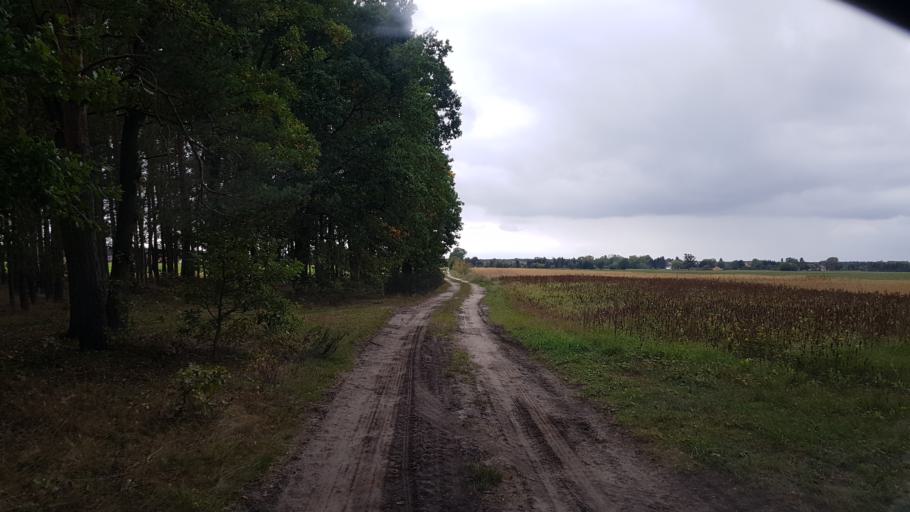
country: DE
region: Brandenburg
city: Finsterwalde
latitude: 51.5772
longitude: 13.6720
